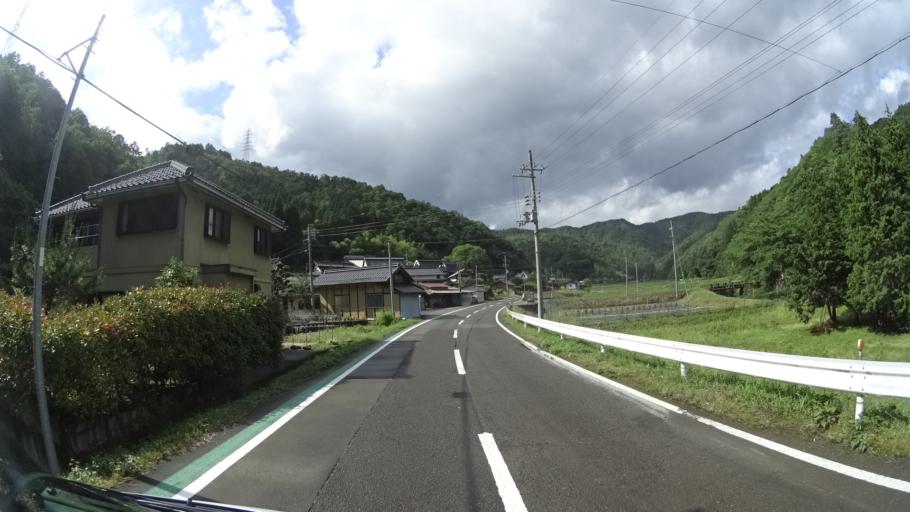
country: JP
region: Kyoto
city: Ayabe
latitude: 35.3850
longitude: 135.2572
